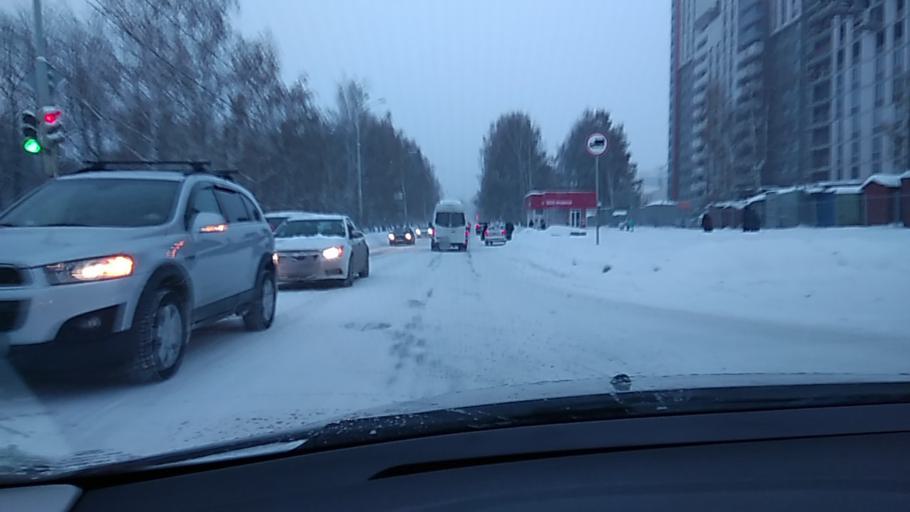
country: RU
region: Sverdlovsk
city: Sovkhoznyy
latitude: 56.8144
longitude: 60.5705
